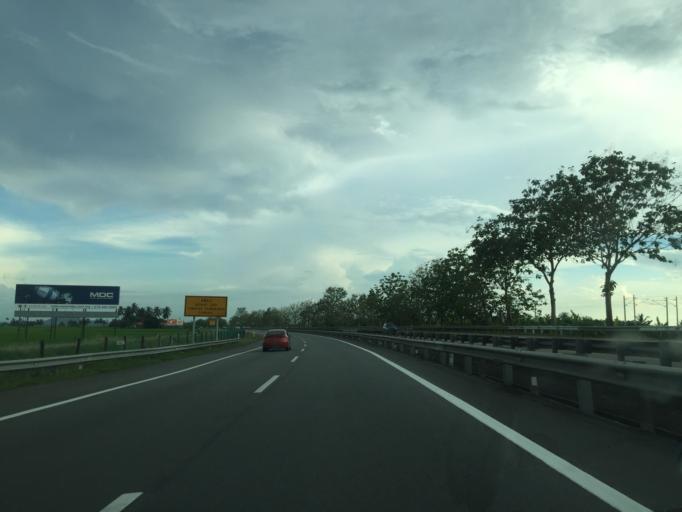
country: MY
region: Kedah
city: Alor Setar
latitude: 6.0192
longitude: 100.4150
